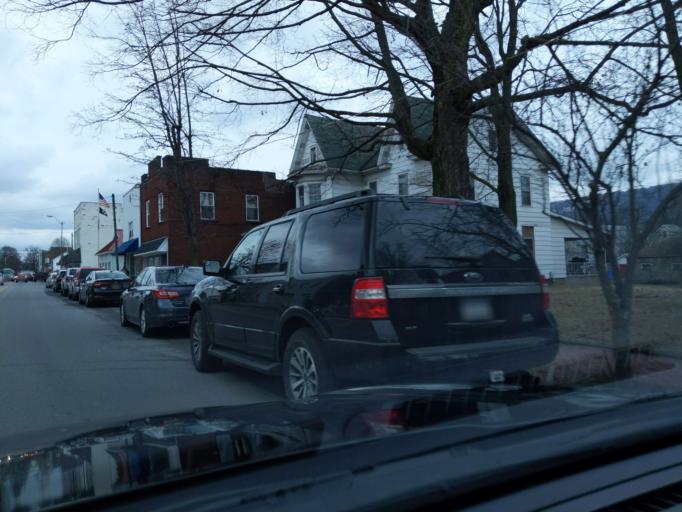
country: US
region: Pennsylvania
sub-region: Blair County
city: Bellwood
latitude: 40.5993
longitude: -78.3338
